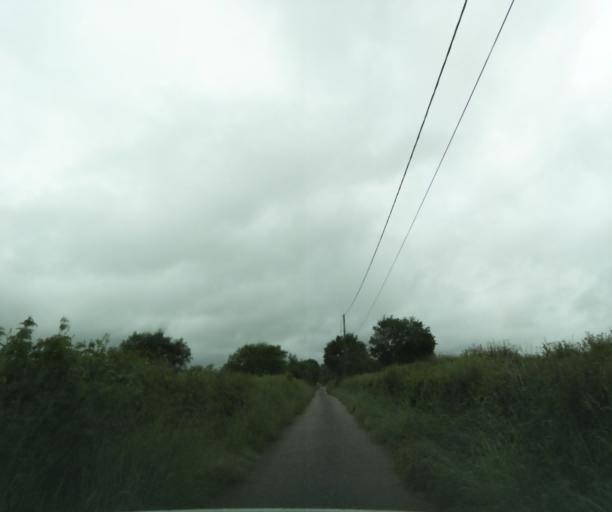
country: FR
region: Bourgogne
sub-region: Departement de Saone-et-Loire
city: Ciry-le-Noble
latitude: 46.5157
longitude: 4.3772
